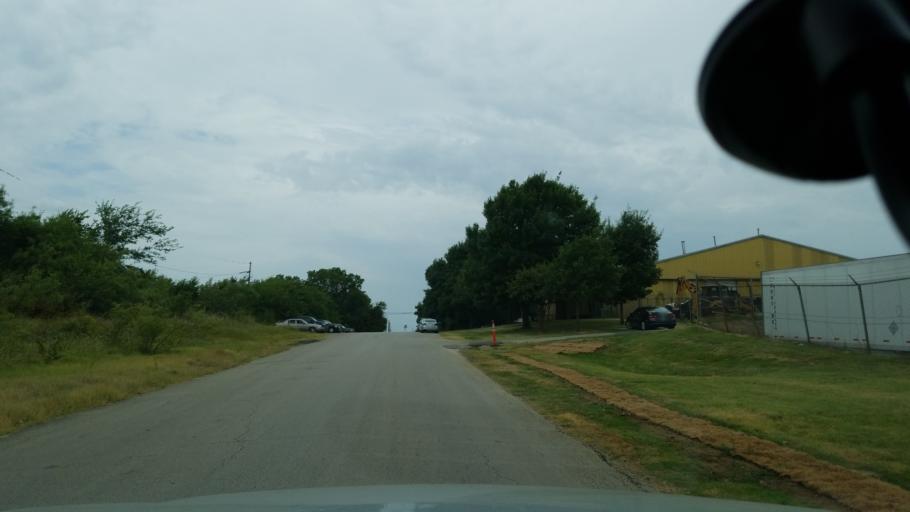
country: US
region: Texas
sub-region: Dallas County
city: Grand Prairie
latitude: 32.7349
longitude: -96.9836
